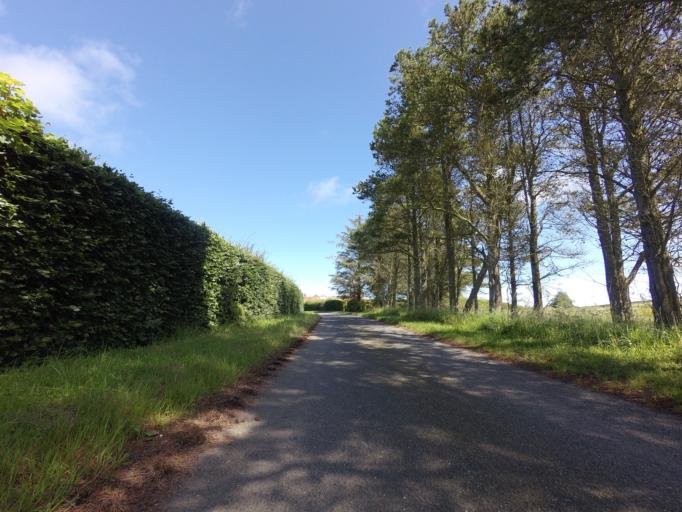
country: GB
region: Scotland
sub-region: Aberdeenshire
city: Banff
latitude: 57.6155
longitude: -2.5086
